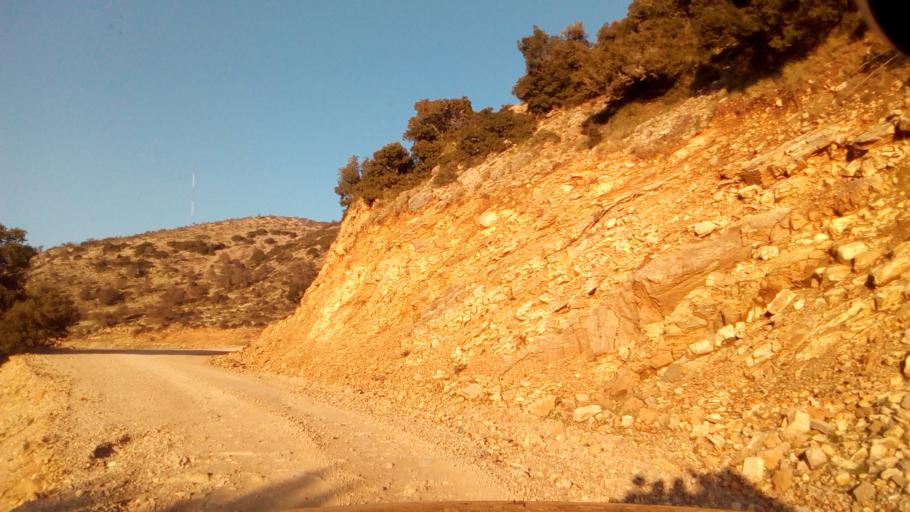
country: GR
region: West Greece
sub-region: Nomos Aitolias kai Akarnanias
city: Nafpaktos
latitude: 38.4488
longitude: 21.8437
